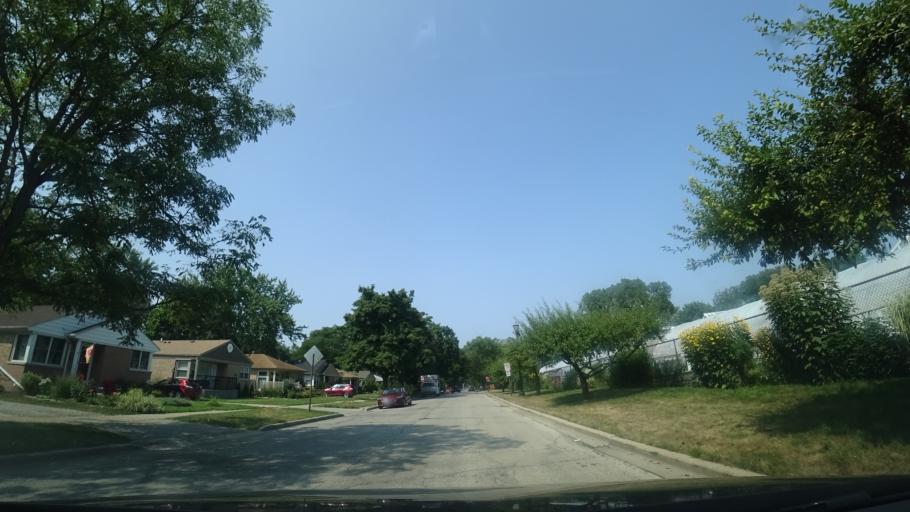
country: US
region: Illinois
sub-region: Cook County
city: Evanston
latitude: 42.0231
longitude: -87.6953
